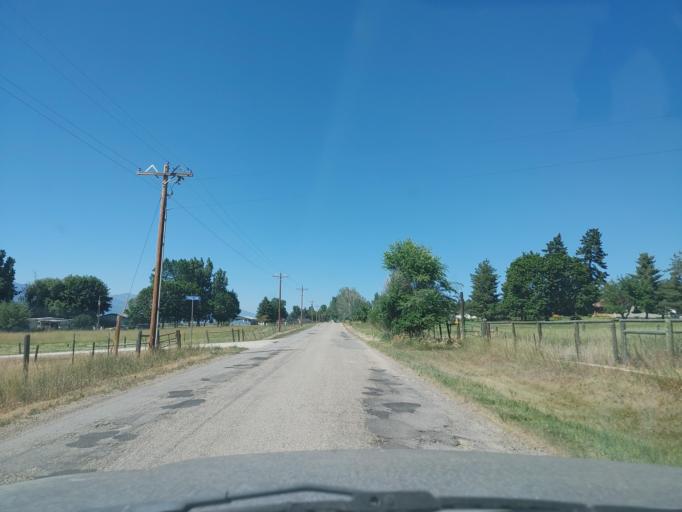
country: US
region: Montana
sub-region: Ravalli County
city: Hamilton
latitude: 46.3359
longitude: -114.0614
